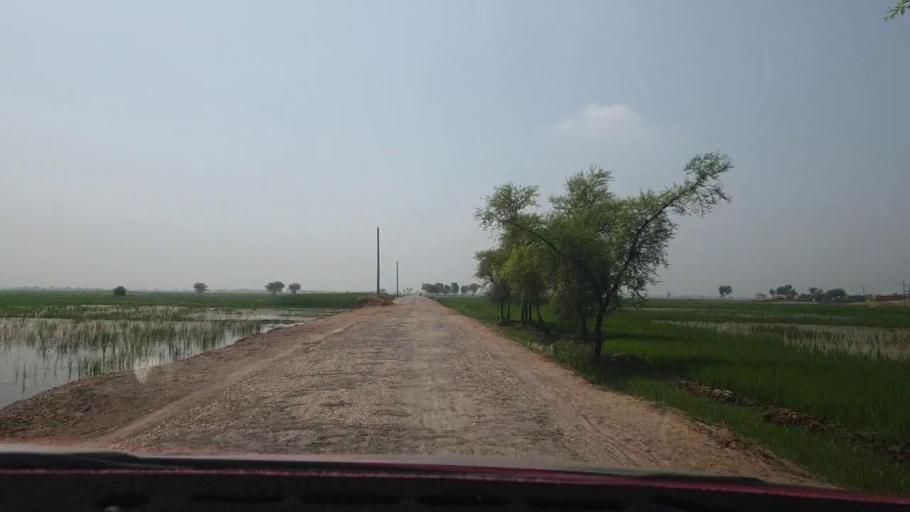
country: PK
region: Sindh
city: Warah
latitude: 27.4015
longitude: 67.8485
